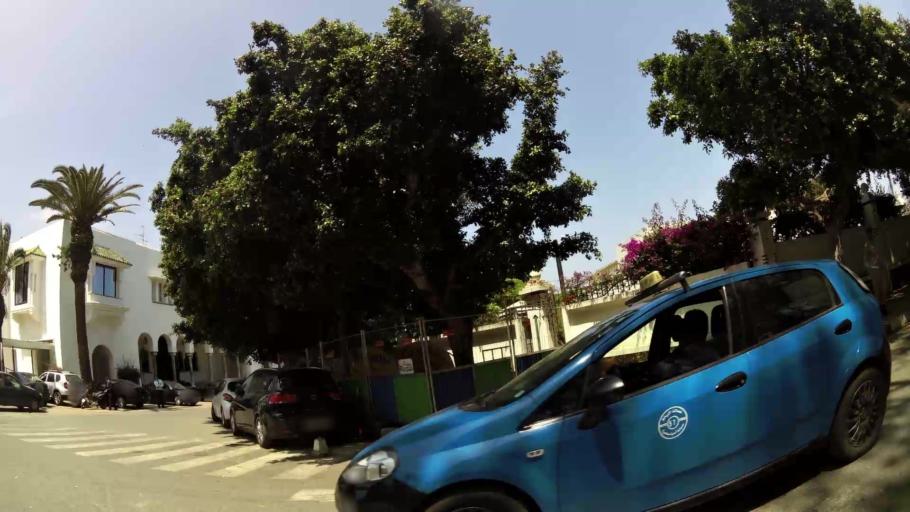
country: MA
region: Rabat-Sale-Zemmour-Zaer
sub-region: Rabat
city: Rabat
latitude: 34.0096
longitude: -6.8266
